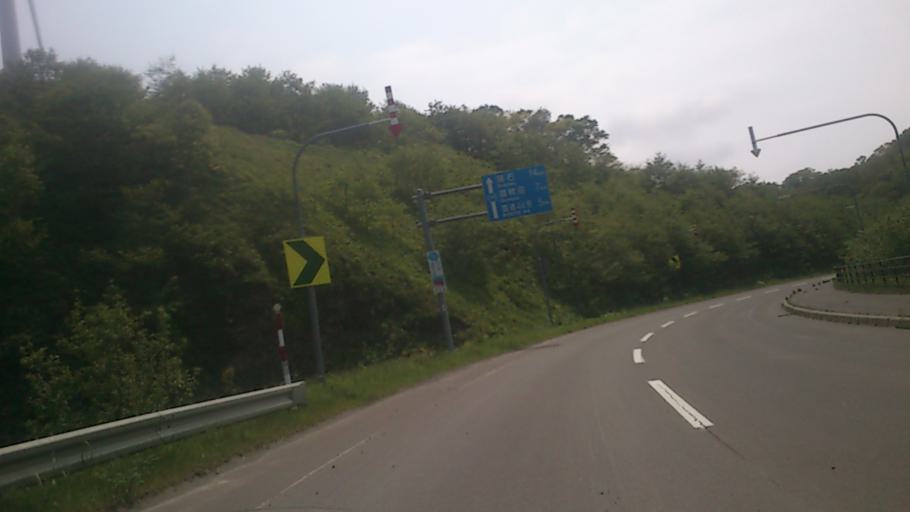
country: JP
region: Hokkaido
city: Nemuro
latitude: 43.2784
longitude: 145.5615
